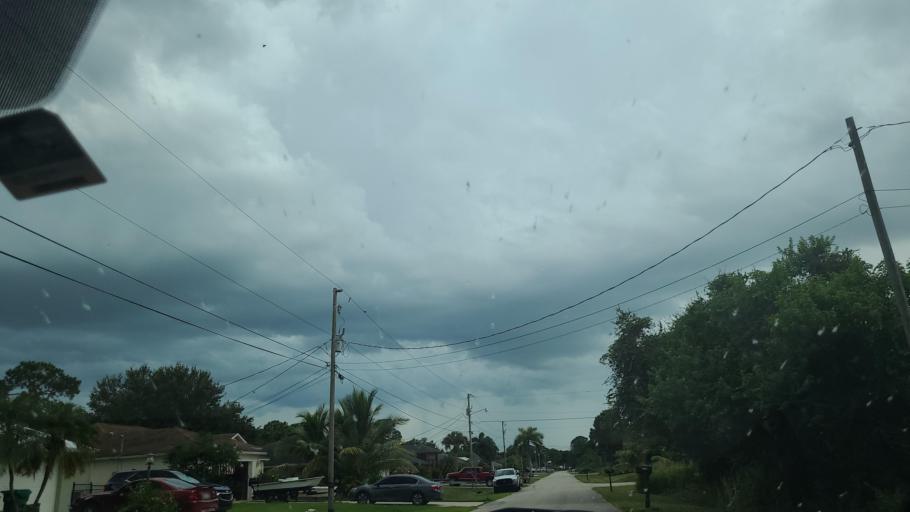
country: US
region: Florida
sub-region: Saint Lucie County
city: Port Saint Lucie
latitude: 27.2528
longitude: -80.4024
